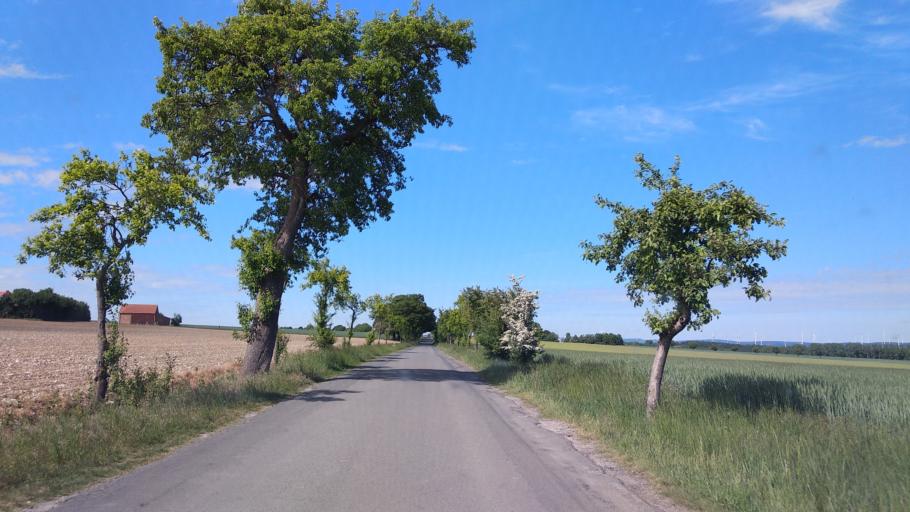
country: DE
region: North Rhine-Westphalia
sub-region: Regierungsbezirk Detmold
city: Paderborn
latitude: 51.6731
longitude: 8.7680
